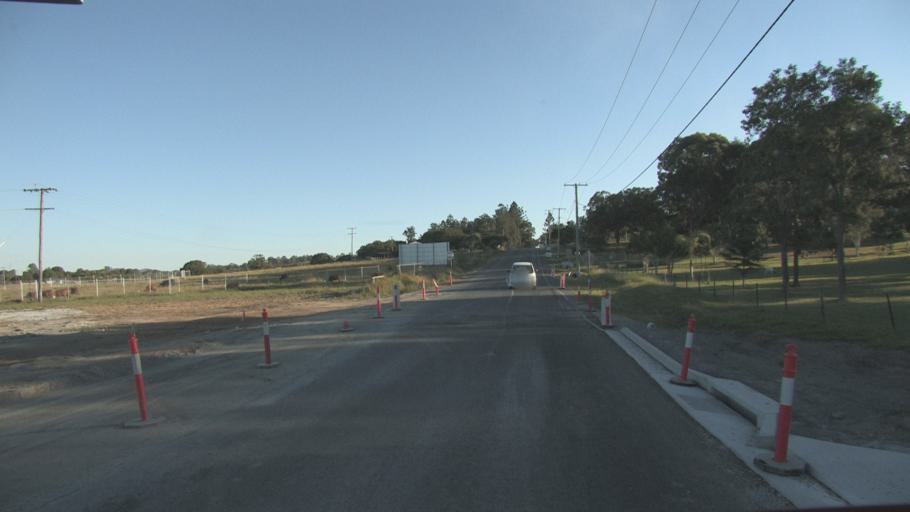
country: AU
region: Queensland
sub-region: Logan
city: Logan Reserve
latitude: -27.7173
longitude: 153.1146
